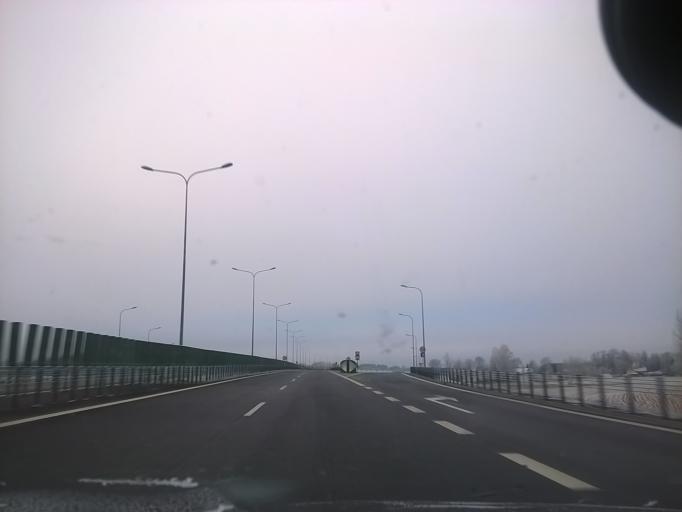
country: PL
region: Warmian-Masurian Voivodeship
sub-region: Powiat olsztynski
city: Biskupiec
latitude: 53.8310
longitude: 21.0707
